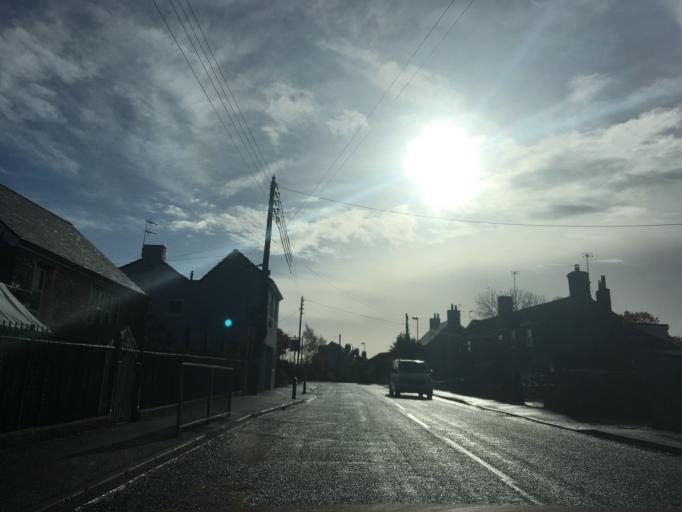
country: GB
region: England
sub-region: South Gloucestershire
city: Yate
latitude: 51.5520
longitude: -2.4358
